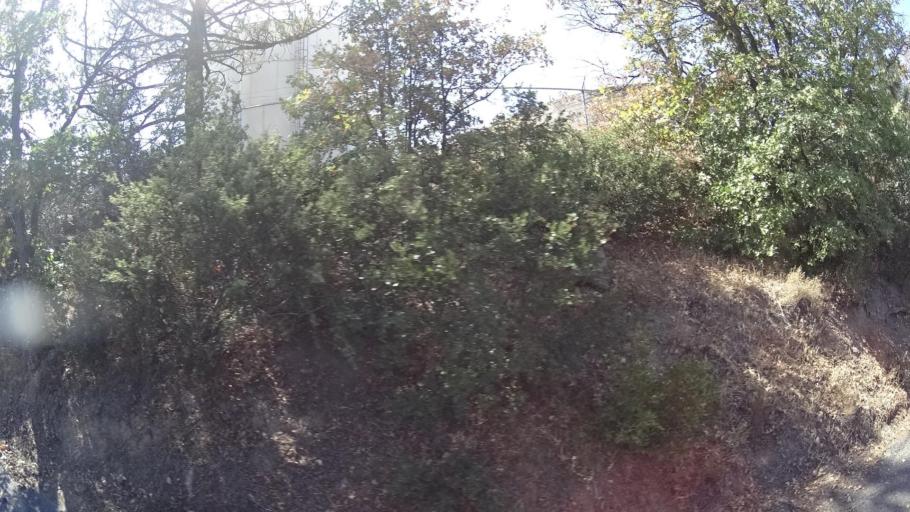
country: US
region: California
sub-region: San Diego County
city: Julian
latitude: 33.0824
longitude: -116.5852
